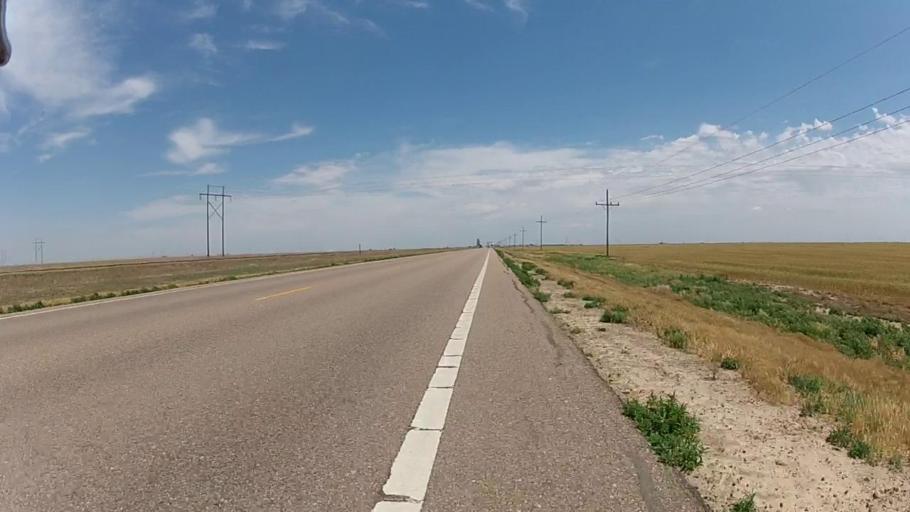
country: US
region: Kansas
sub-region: Haskell County
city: Sublette
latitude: 37.4683
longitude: -100.8975
